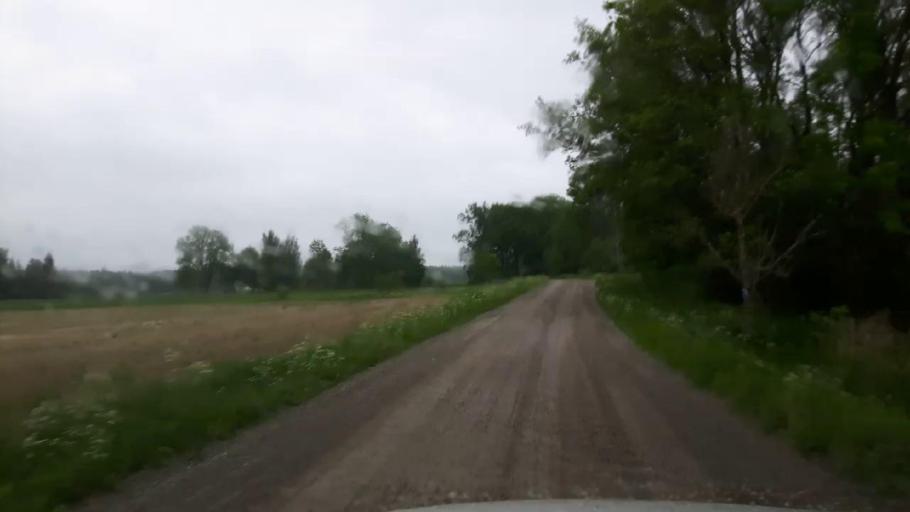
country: SE
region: Vaestmanland
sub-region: Arboga Kommun
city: Tyringe
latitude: 59.3940
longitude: 15.9253
